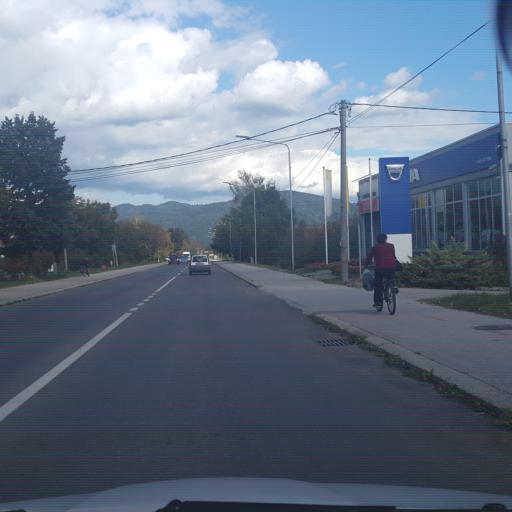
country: RS
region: Central Serbia
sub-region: Raski Okrug
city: Vrnjacka Banja
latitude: 43.6320
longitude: 20.9042
